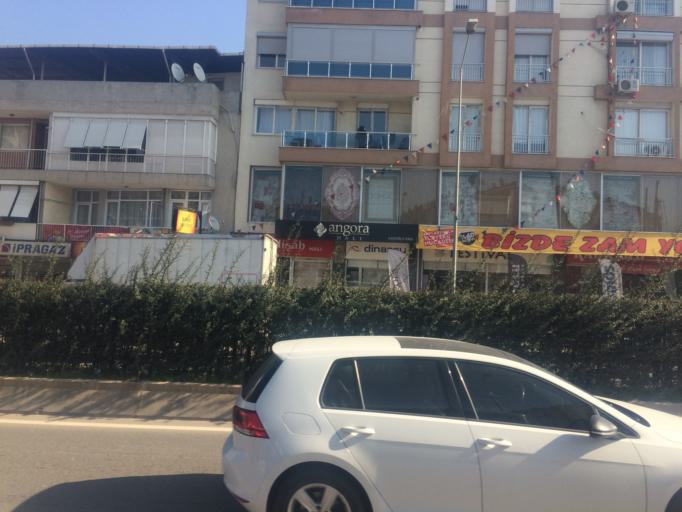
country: TR
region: Izmir
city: Karsiyaka
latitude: 38.5005
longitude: 27.0546
